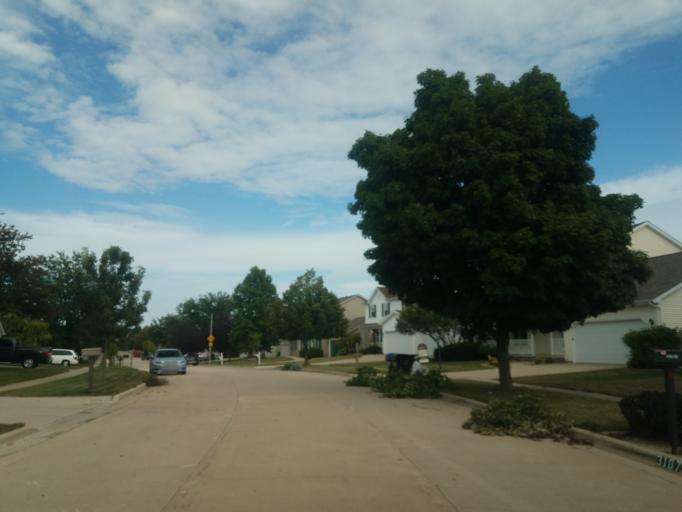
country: US
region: Illinois
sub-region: McLean County
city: Normal
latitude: 40.4984
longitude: -88.9229
